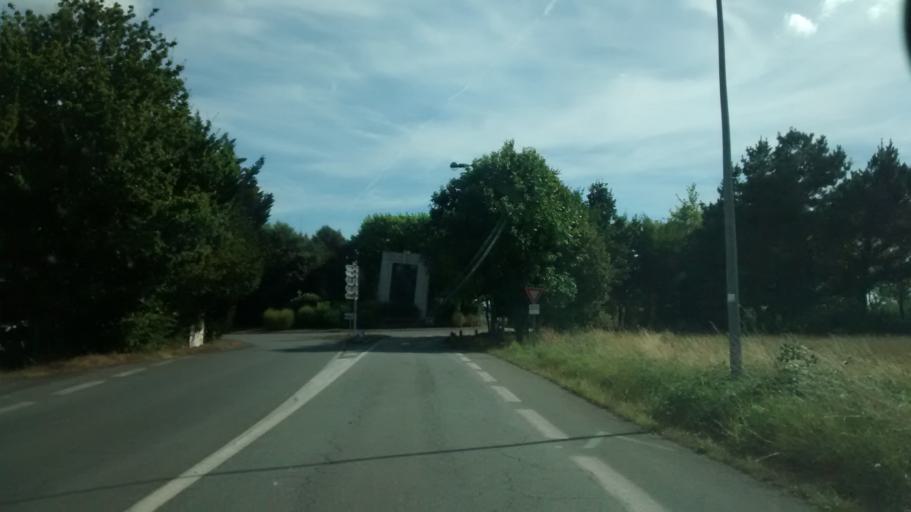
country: FR
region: Pays de la Loire
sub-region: Departement de la Loire-Atlantique
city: Pont-Saint-Martin
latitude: 47.1454
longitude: -1.6039
